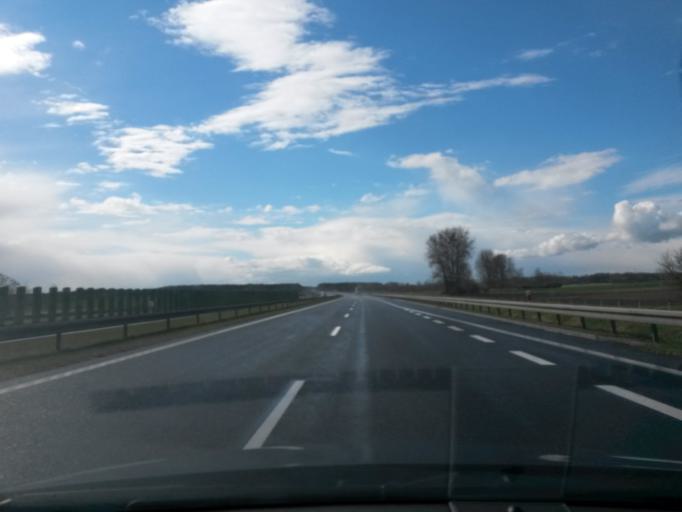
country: PL
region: Greater Poland Voivodeship
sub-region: Powiat slupecki
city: Strzalkowo
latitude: 52.2611
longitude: 17.7820
